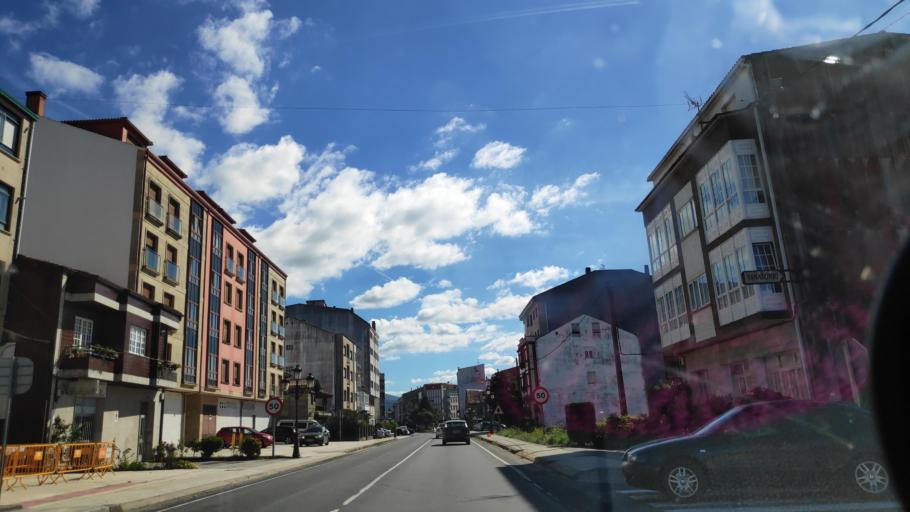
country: ES
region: Galicia
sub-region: Provincia da Coruna
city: Padron
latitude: 42.7417
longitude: -8.6580
